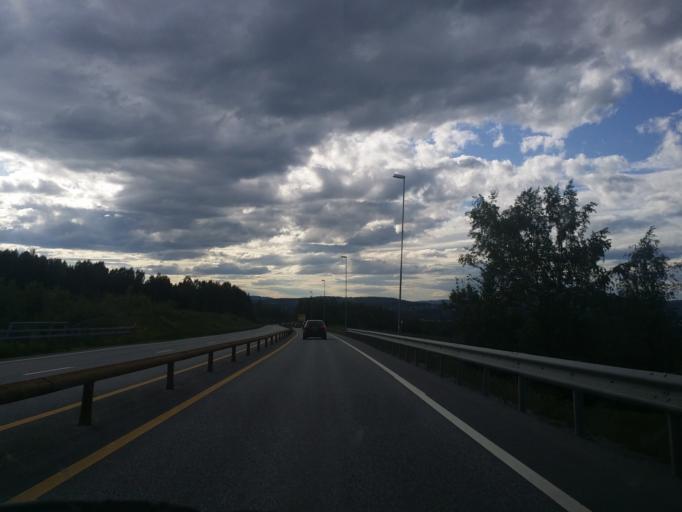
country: NO
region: Hedmark
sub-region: Stange
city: Stange
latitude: 60.7792
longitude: 11.1453
